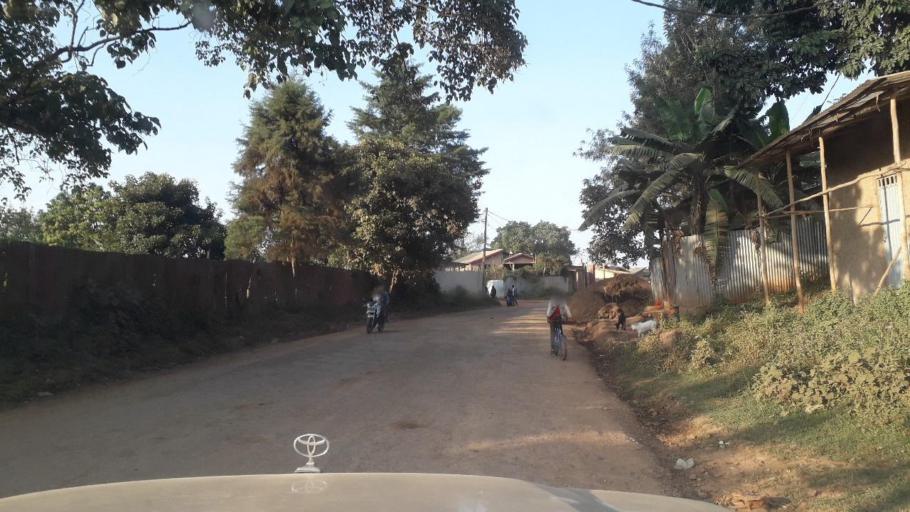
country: ET
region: Oromiya
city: Jima
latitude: 7.6370
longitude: 36.8365
